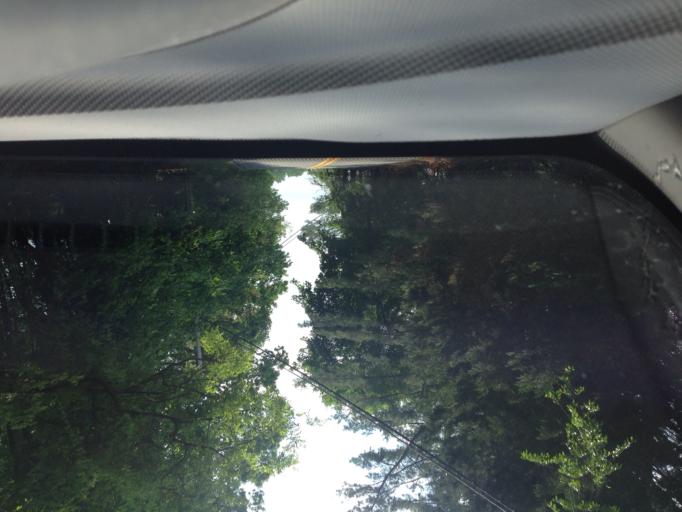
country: US
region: Maryland
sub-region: Baltimore County
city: Cockeysville
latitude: 39.4833
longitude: -76.6746
